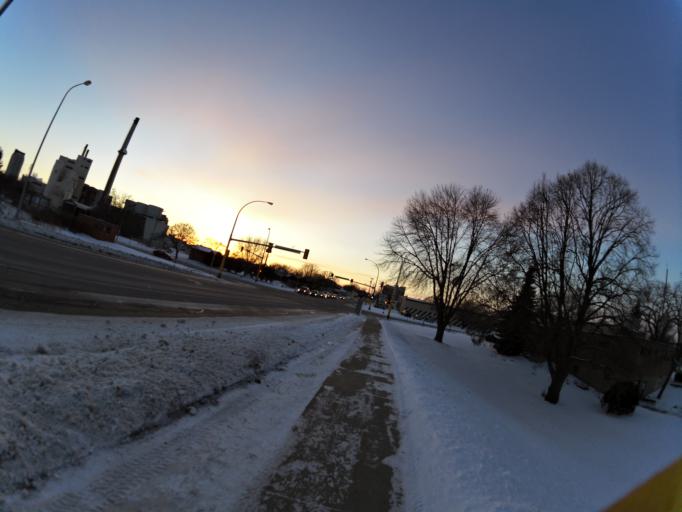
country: US
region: Minnesota
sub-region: Olmsted County
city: Rochester
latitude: 44.0305
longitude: -92.4584
